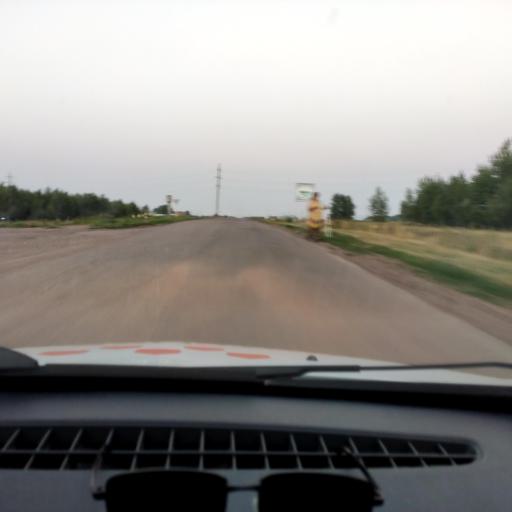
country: RU
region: Bashkortostan
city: Ulukulevo
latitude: 54.3707
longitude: 56.4219
